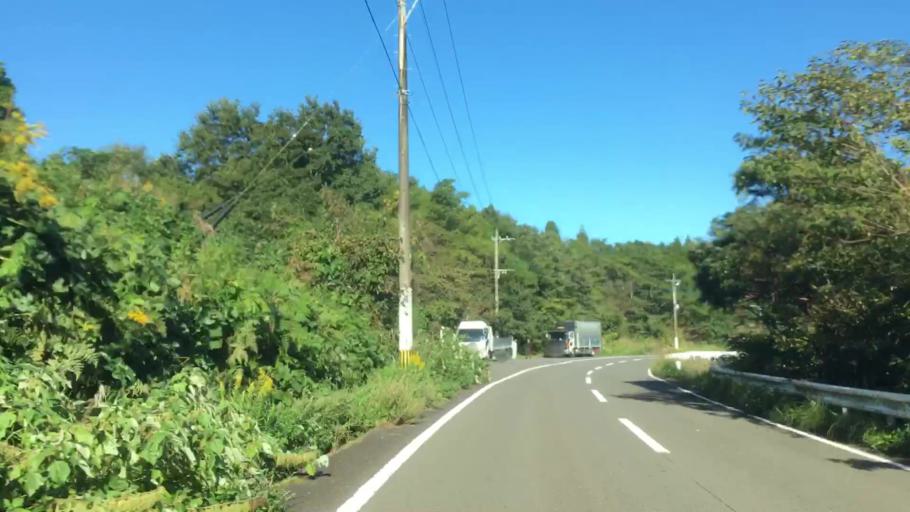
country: JP
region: Nagasaki
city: Sasebo
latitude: 33.0337
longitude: 129.6862
